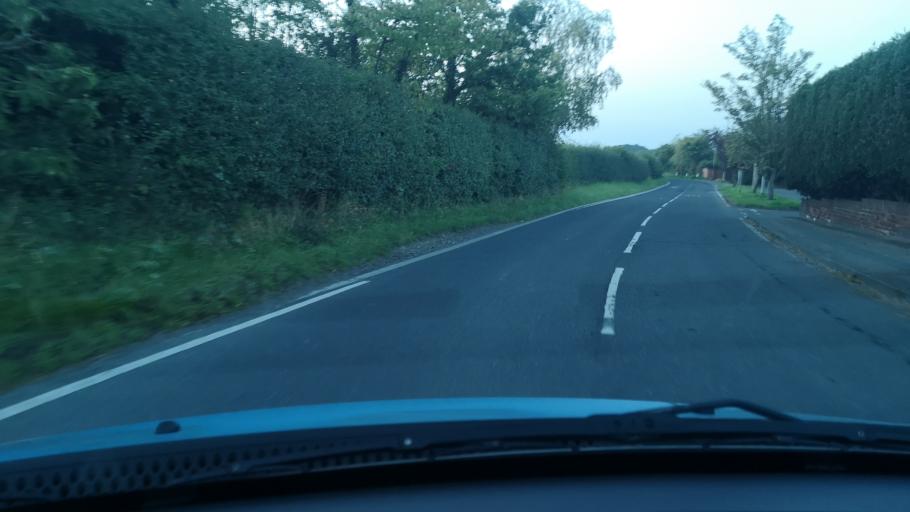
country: GB
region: England
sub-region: City and Borough of Wakefield
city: Low Ackworth
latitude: 53.6526
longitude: -1.3160
